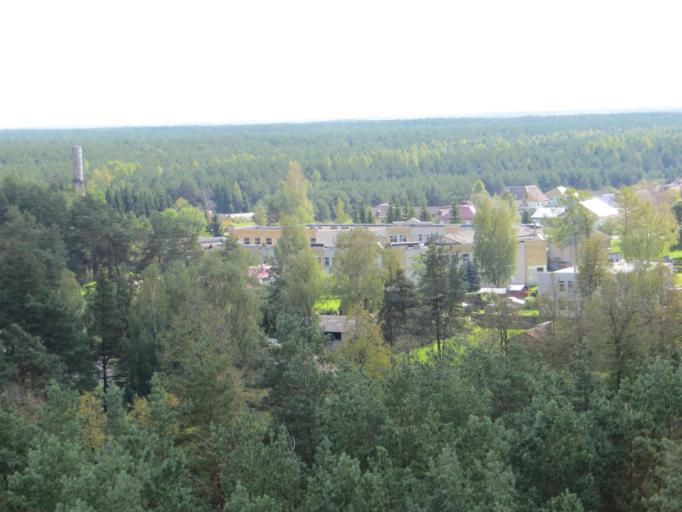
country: LT
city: Trakai
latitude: 54.5059
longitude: 24.9826
